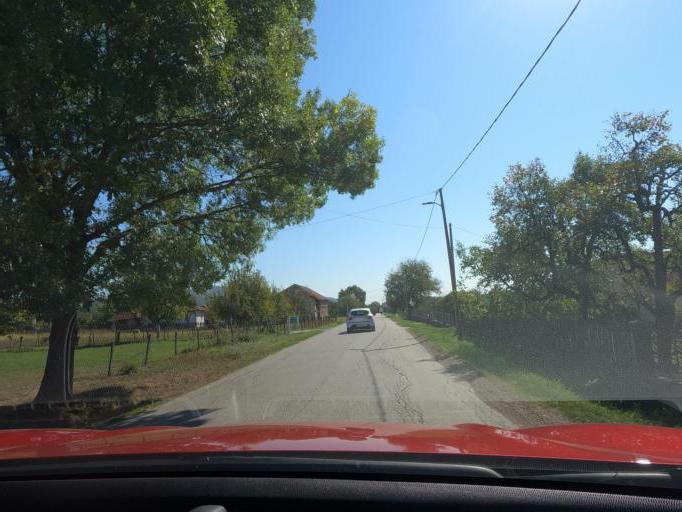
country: RS
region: Central Serbia
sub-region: Raski Okrug
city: Kraljevo
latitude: 43.7582
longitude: 20.6841
